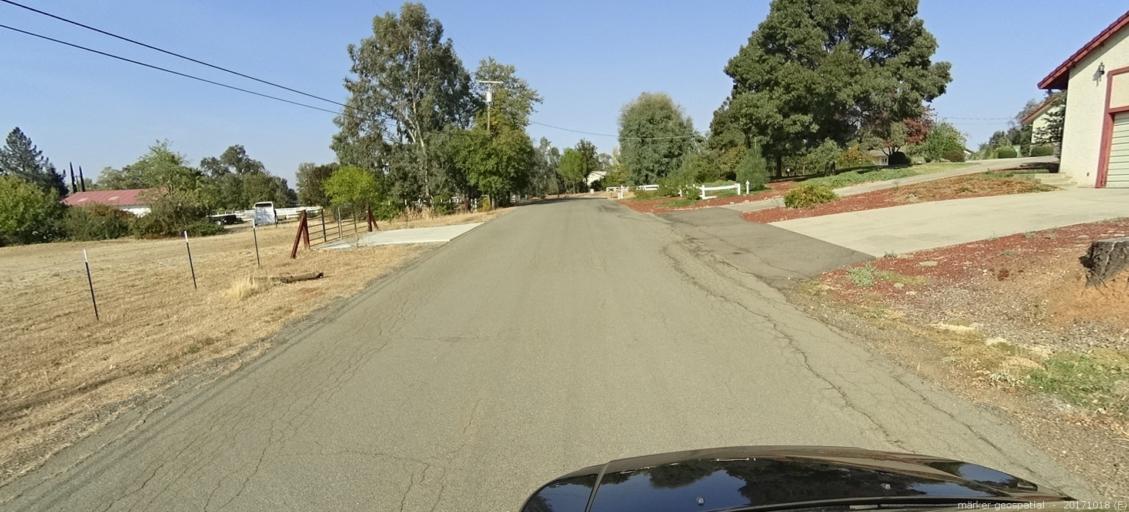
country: US
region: California
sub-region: Shasta County
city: Palo Cedro
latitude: 40.5760
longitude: -122.2356
